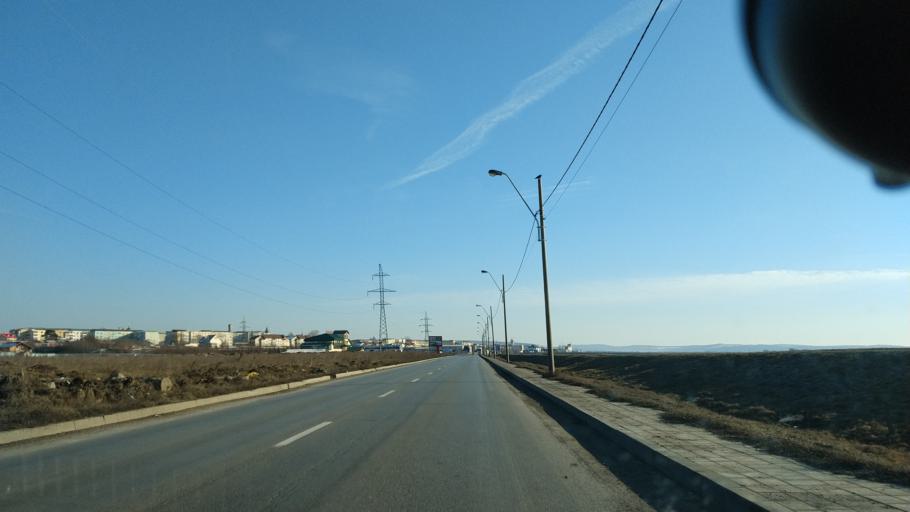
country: RO
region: Neamt
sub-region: Municipiul Roman
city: Roman
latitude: 46.9222
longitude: 26.9125
